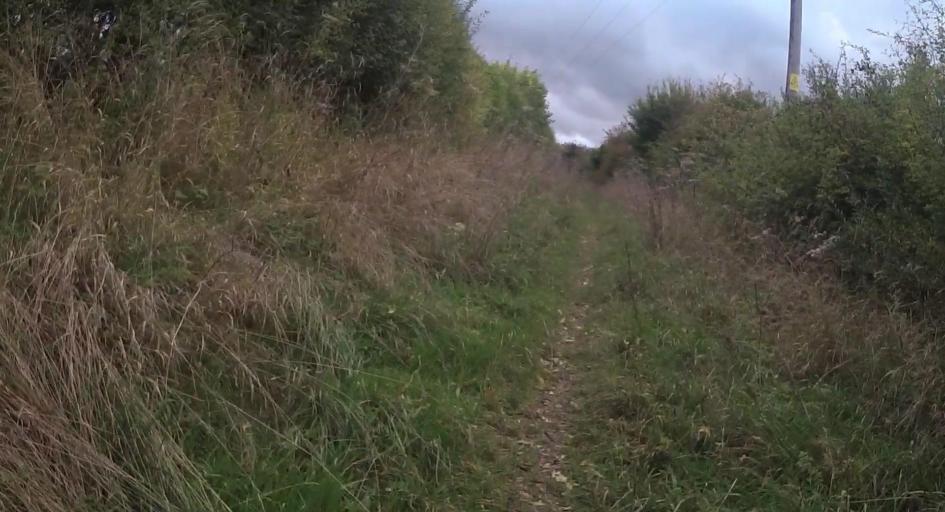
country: GB
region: England
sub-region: Hampshire
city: Andover
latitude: 51.1588
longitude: -1.4010
